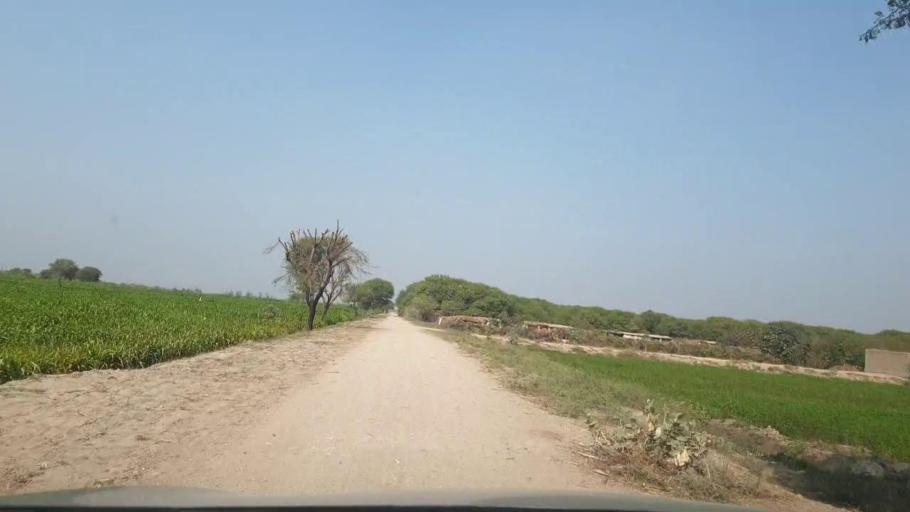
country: PK
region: Sindh
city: Tando Allahyar
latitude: 25.5638
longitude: 68.8255
